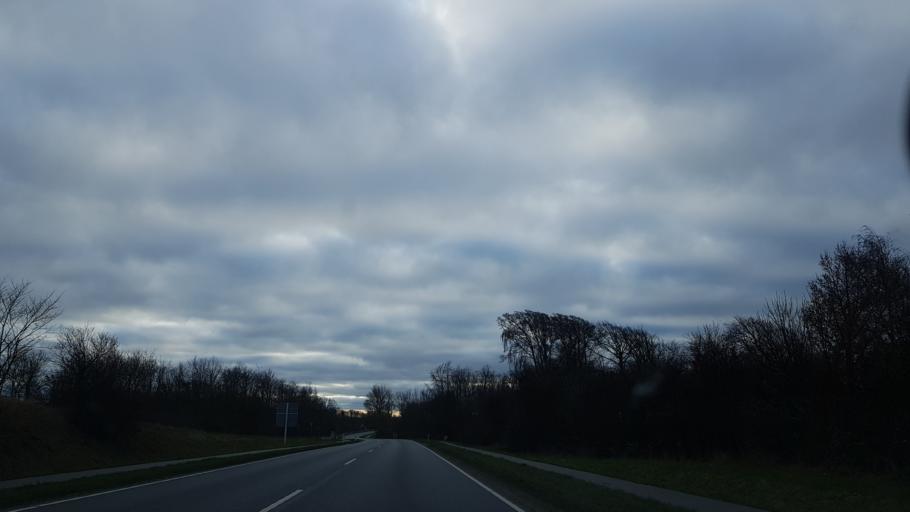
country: DK
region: Zealand
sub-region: Kalundborg Kommune
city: Gorlev
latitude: 55.5694
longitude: 11.1952
